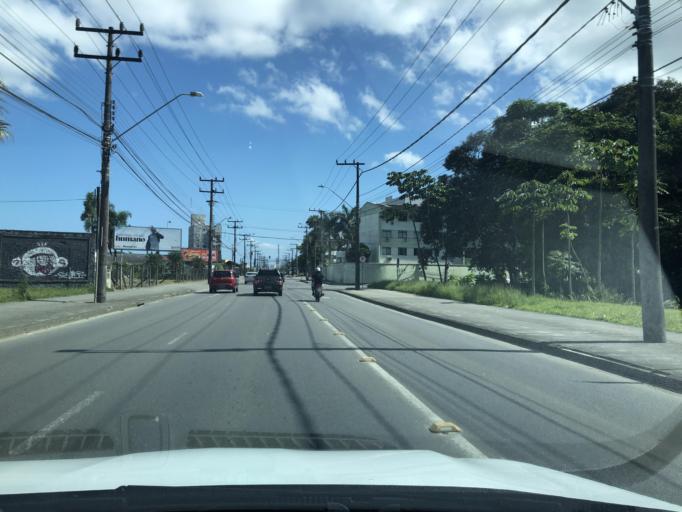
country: BR
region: Santa Catarina
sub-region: Joinville
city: Joinville
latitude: -26.2623
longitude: -48.8513
